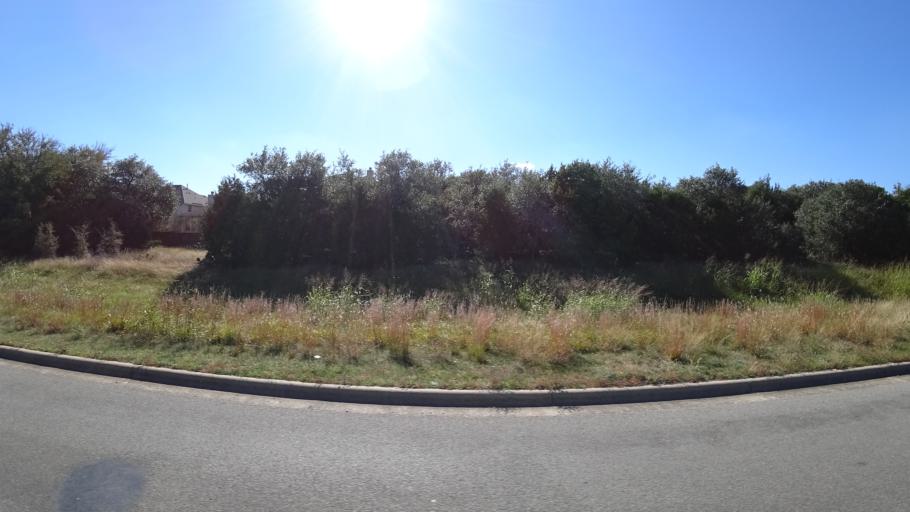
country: US
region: Texas
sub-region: Travis County
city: Shady Hollow
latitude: 30.1902
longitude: -97.9207
